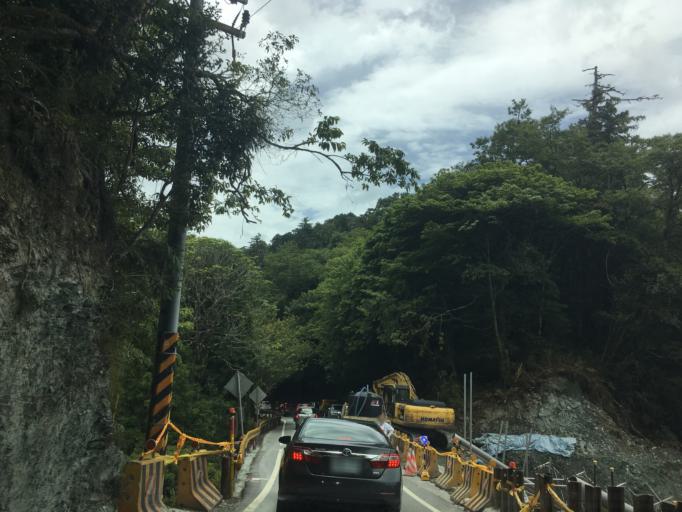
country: TW
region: Taiwan
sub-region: Hualien
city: Hualian
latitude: 24.1762
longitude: 121.3853
